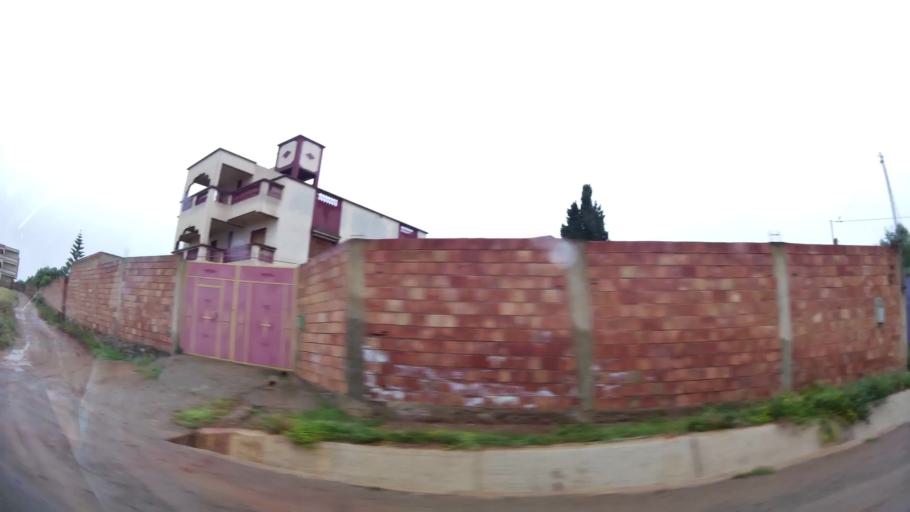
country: MA
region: Oriental
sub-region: Nador
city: Boudinar
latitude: 35.1210
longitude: -3.5742
